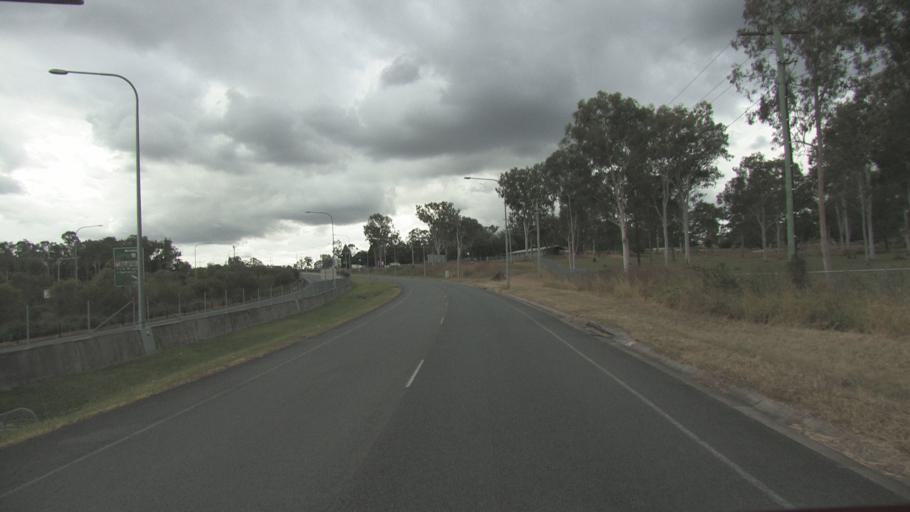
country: AU
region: Queensland
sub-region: Logan
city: Park Ridge South
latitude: -27.7120
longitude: 153.0370
